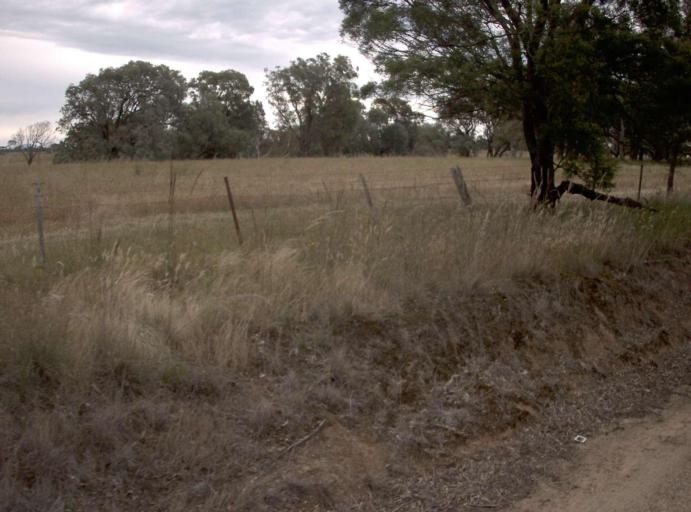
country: AU
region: Victoria
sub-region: Wellington
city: Sale
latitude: -38.0089
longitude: 147.1896
